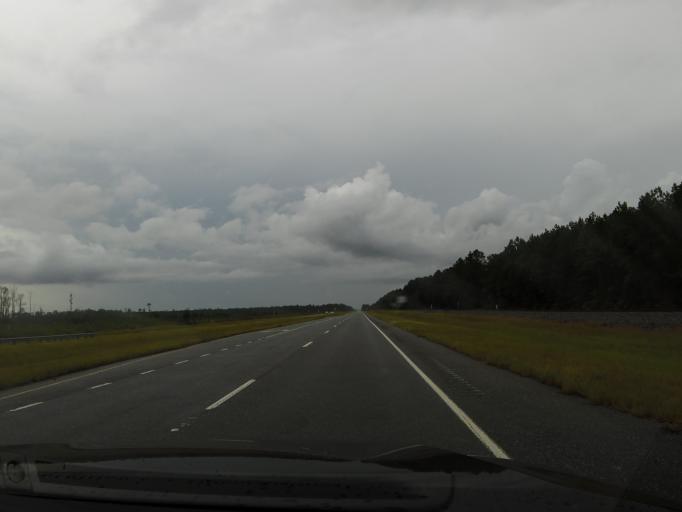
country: US
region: Georgia
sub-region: Wayne County
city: Jesup
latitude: 31.5024
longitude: -81.7572
